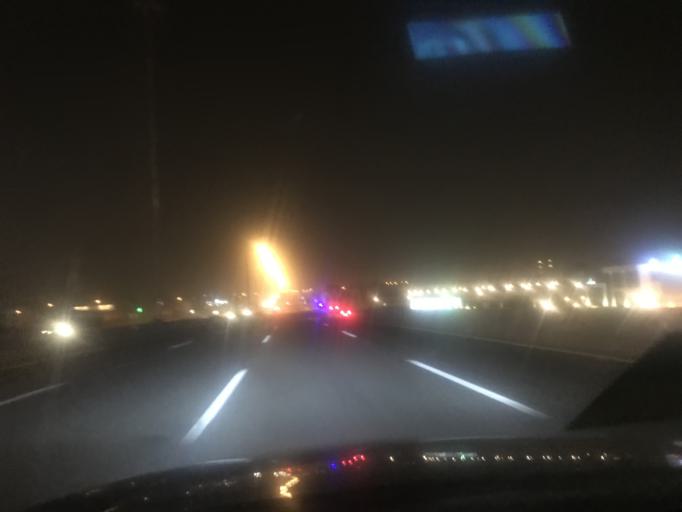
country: SA
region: Ar Riyad
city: Riyadh
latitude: 24.7734
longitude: 46.5731
